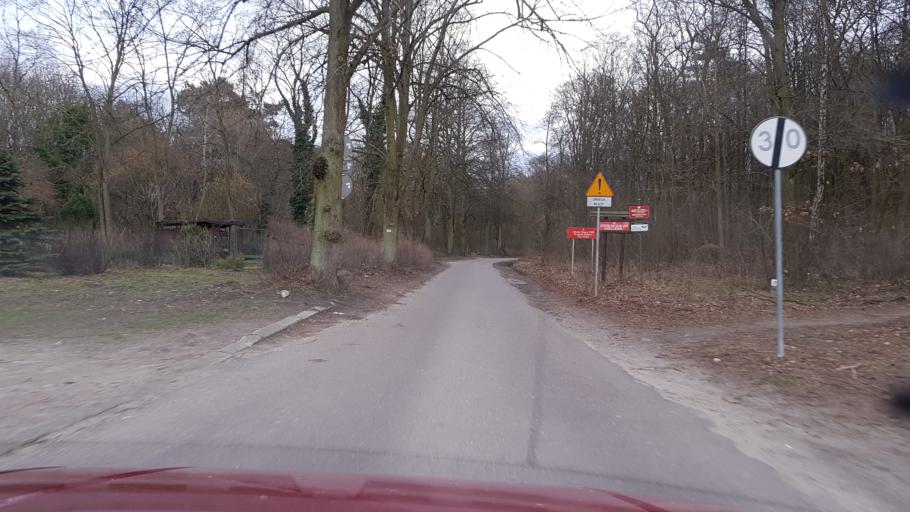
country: PL
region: West Pomeranian Voivodeship
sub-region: Szczecin
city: Szczecin
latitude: 53.3566
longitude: 14.6001
